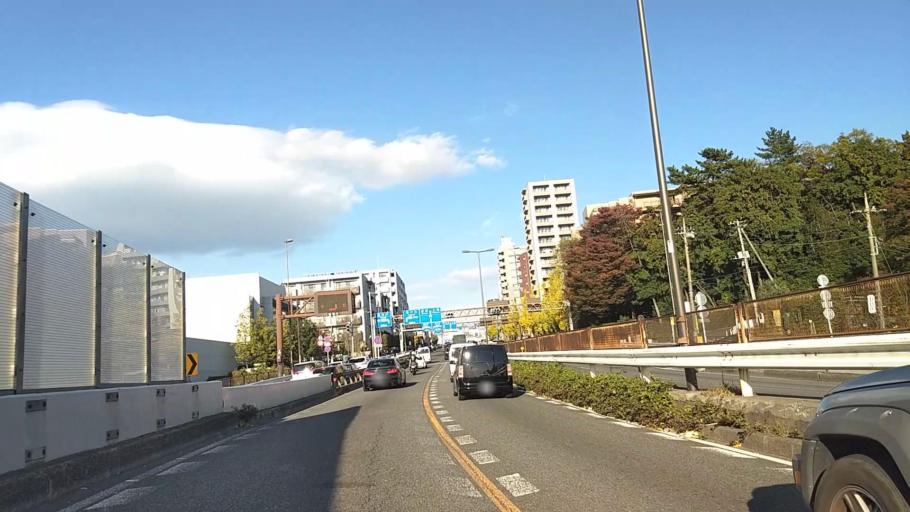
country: JP
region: Tokyo
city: Chofugaoka
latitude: 35.6179
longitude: 139.6283
